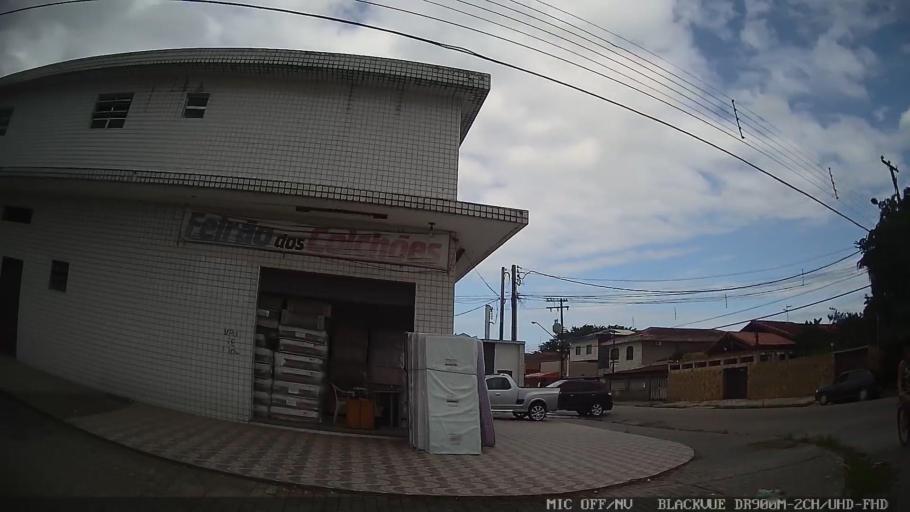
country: BR
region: Sao Paulo
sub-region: Guaruja
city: Guaruja
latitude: -23.9918
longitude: -46.2850
